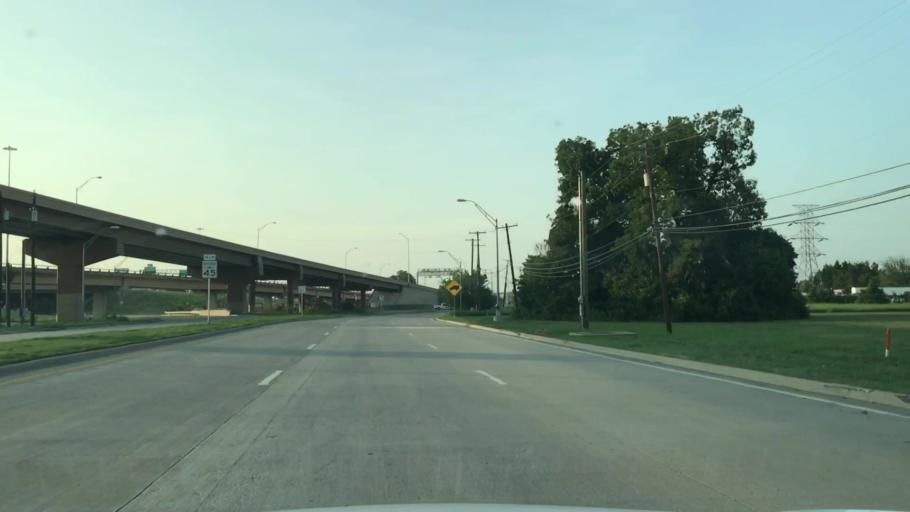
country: US
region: Texas
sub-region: Dallas County
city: Farmers Branch
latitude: 32.9117
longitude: -96.8962
